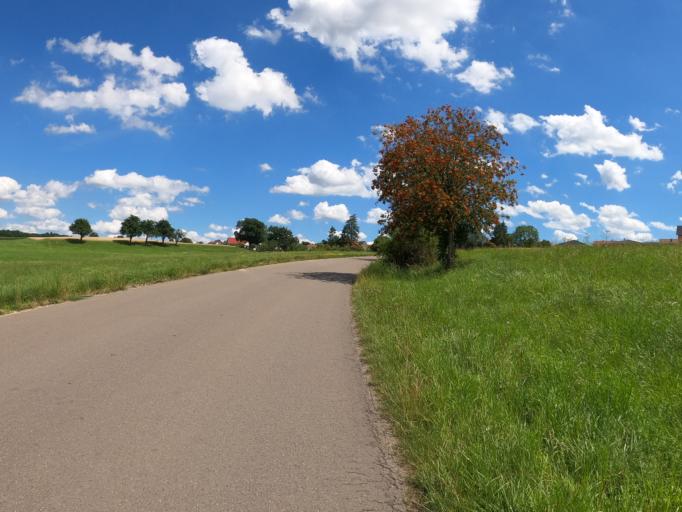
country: DE
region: Bavaria
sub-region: Swabia
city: Leipheim
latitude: 48.4028
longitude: 10.1920
